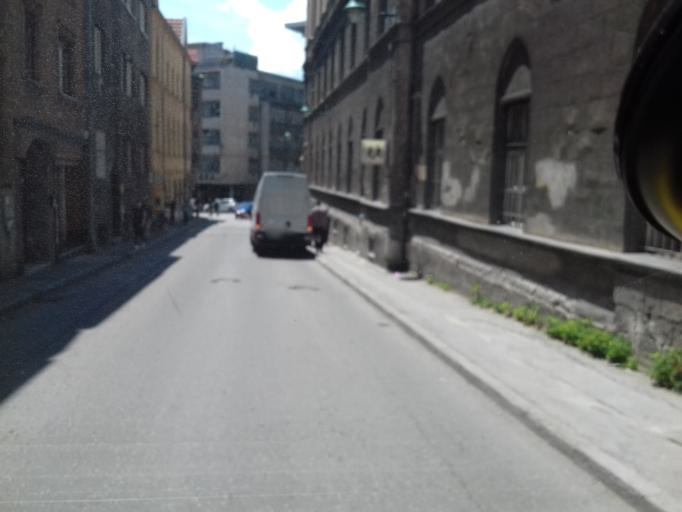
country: BA
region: Federation of Bosnia and Herzegovina
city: Kobilja Glava
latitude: 43.8606
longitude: 18.4254
